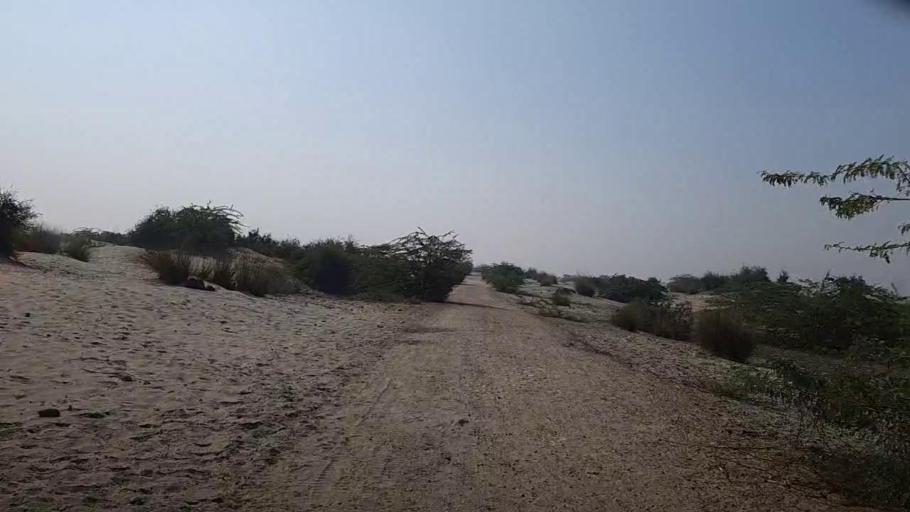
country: PK
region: Sindh
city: Bozdar
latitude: 27.2330
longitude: 68.5948
